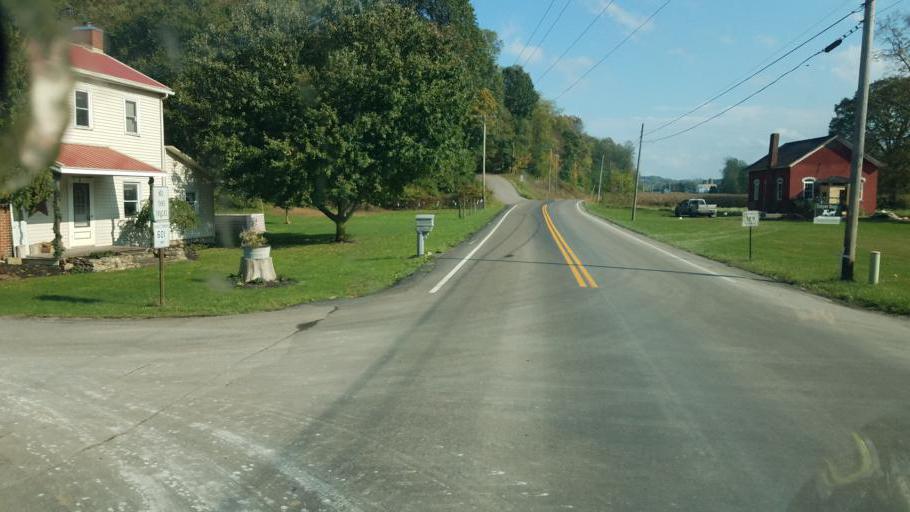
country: US
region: Ohio
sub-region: Holmes County
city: Millersburg
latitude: 40.6149
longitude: -81.8681
